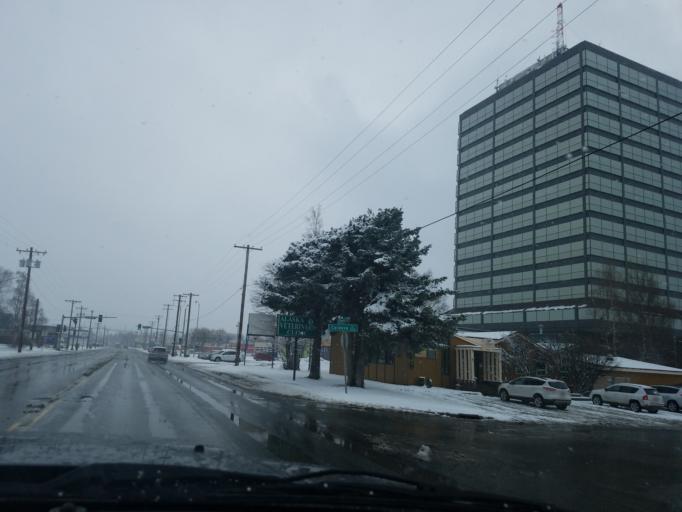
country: US
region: Alaska
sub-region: Anchorage Municipality
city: Anchorage
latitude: 61.1981
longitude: -149.8790
